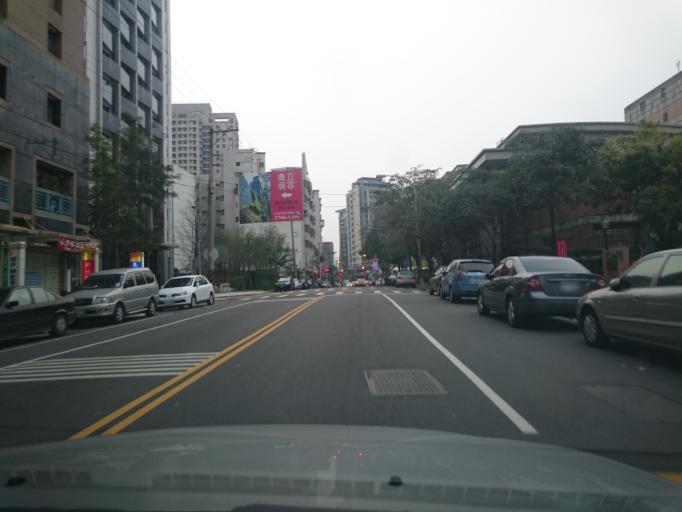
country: TW
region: Taiwan
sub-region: Taichung City
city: Taichung
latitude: 24.1719
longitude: 120.6391
